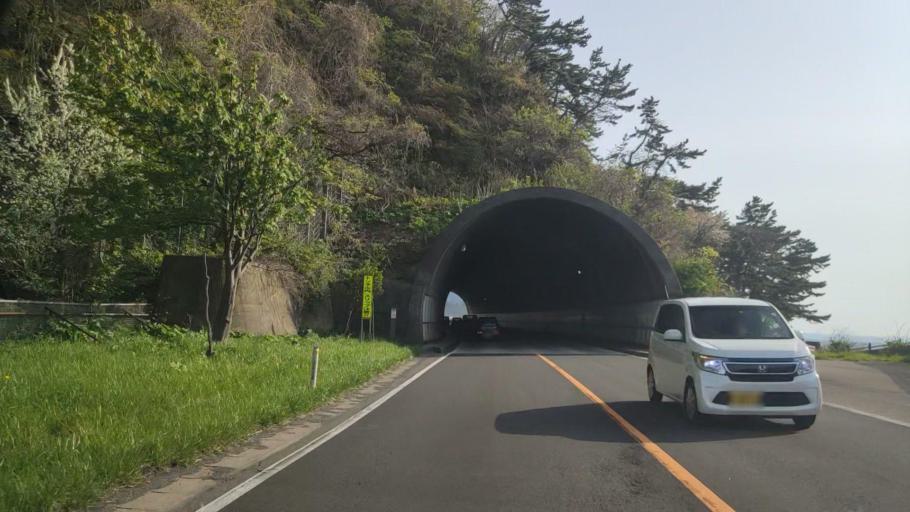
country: JP
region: Aomori
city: Aomori Shi
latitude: 40.8840
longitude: 140.8513
